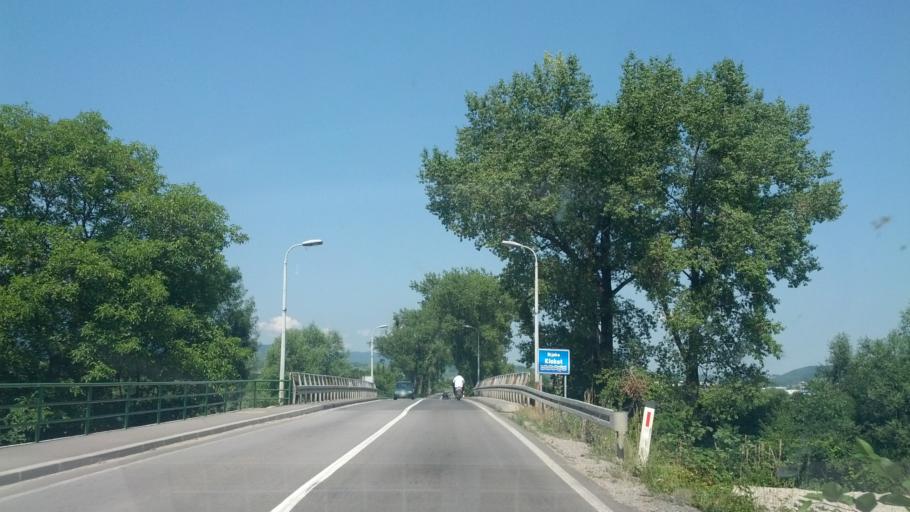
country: BA
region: Federation of Bosnia and Herzegovina
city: Bihac
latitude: 44.8270
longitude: 15.8414
